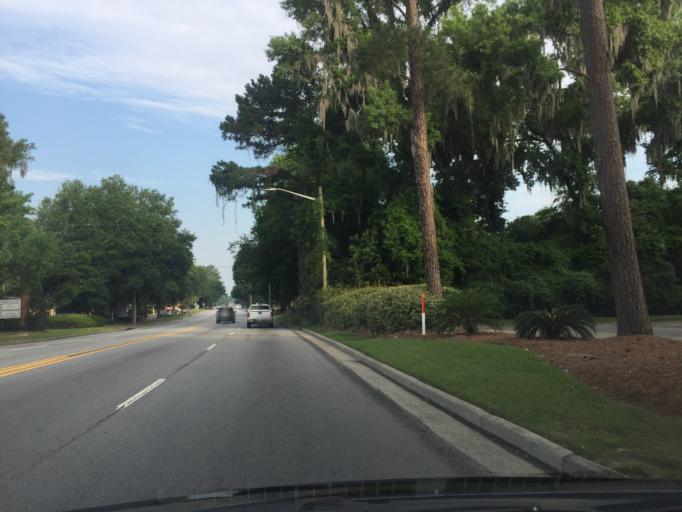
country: US
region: Georgia
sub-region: Chatham County
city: Isle of Hope
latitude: 32.0071
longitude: -81.1025
